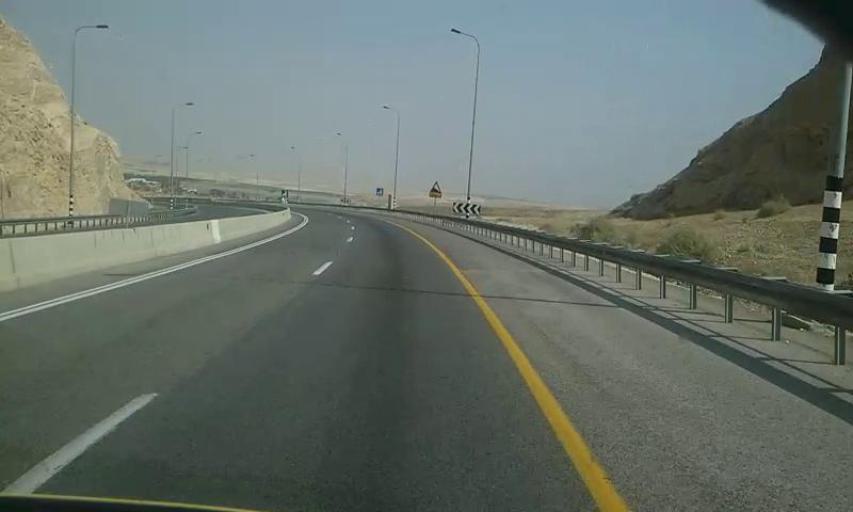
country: PS
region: West Bank
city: Jericho
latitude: 31.7993
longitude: 35.4434
